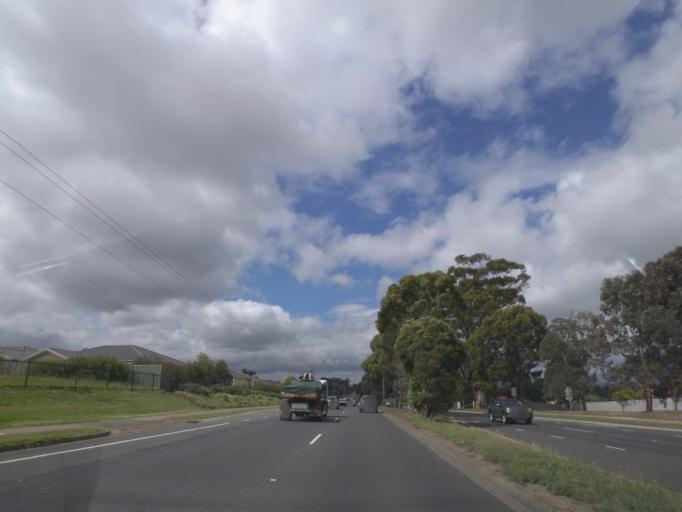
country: AU
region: Victoria
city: Plenty
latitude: -37.6821
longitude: 145.1203
